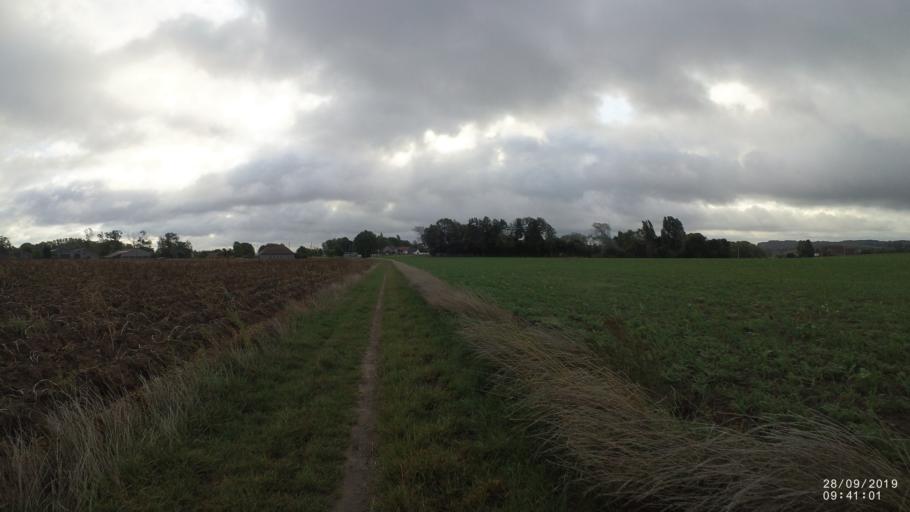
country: BE
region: Wallonia
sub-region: Province du Hainaut
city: Flobecq
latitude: 50.7971
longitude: 3.7103
